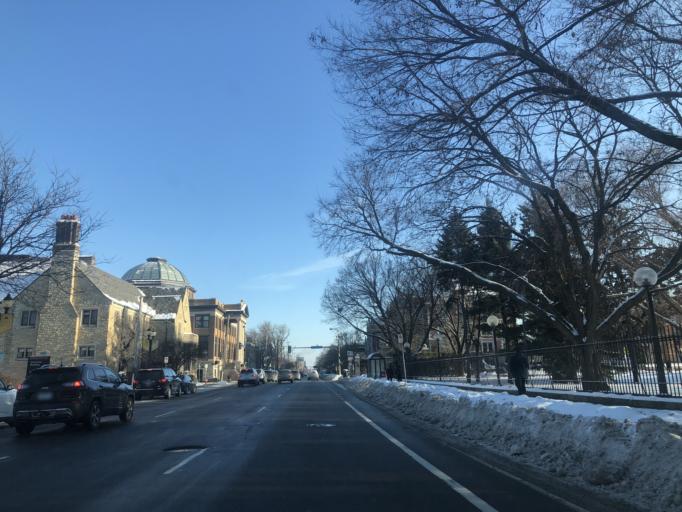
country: US
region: Minnesota
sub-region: Hennepin County
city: Minneapolis
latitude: 44.9794
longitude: -93.2364
